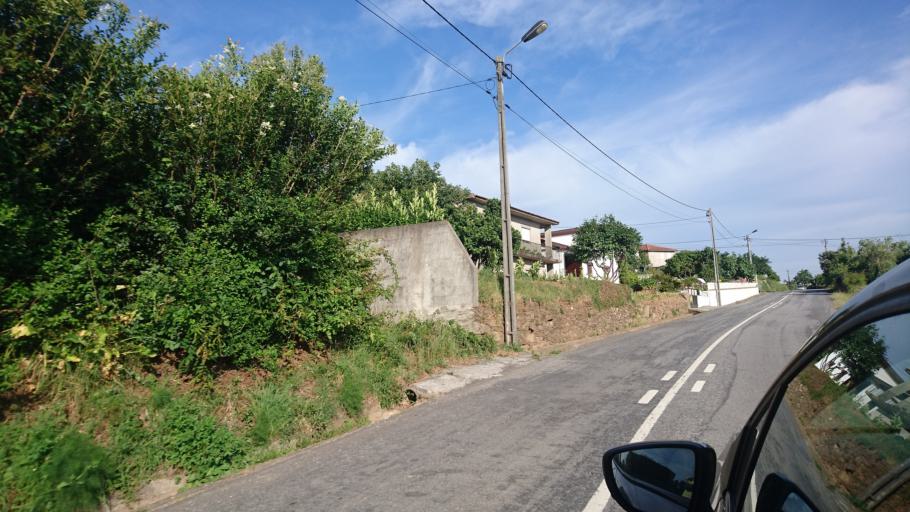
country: PT
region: Porto
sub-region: Paredes
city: Recarei
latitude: 41.1381
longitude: -8.3810
